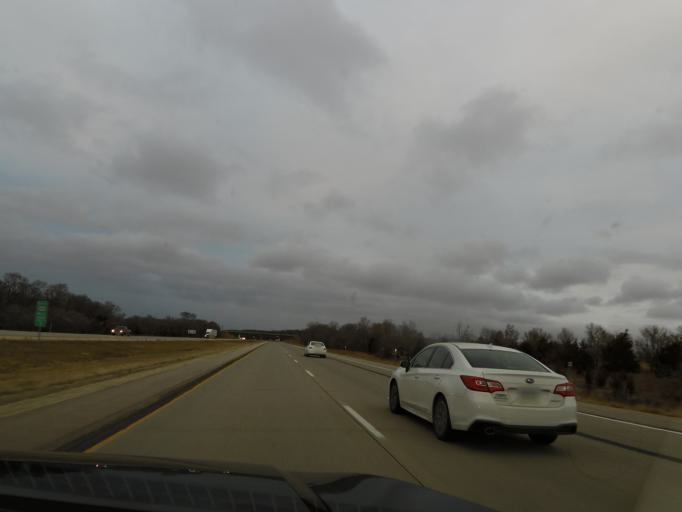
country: US
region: Iowa
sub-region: Black Hawk County
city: Cedar Falls
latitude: 42.5663
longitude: -92.4269
